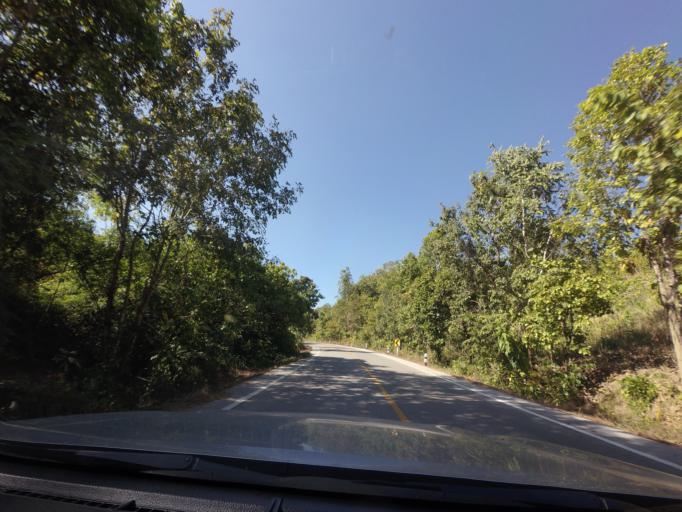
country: TH
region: Lampang
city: Chae Hom
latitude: 18.5618
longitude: 99.6246
